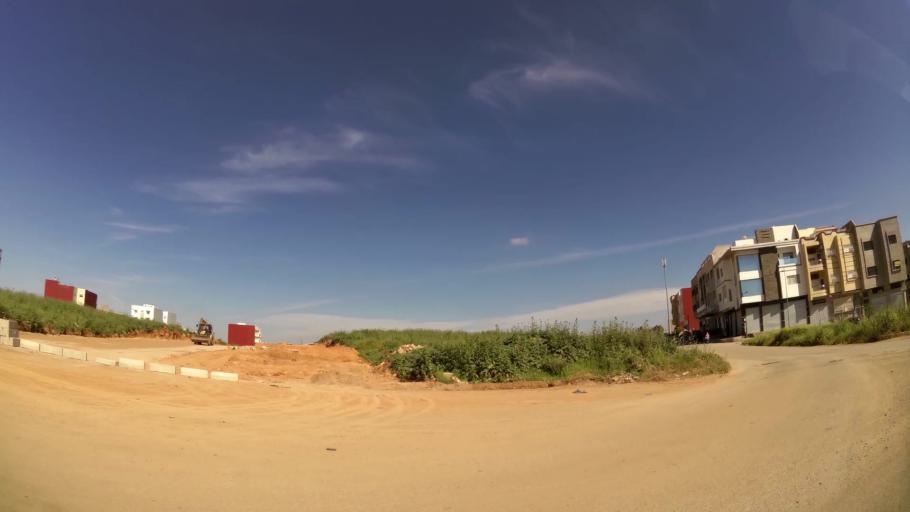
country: MA
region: Fes-Boulemane
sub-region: Fes
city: Fes
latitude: 33.9939
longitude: -5.0054
